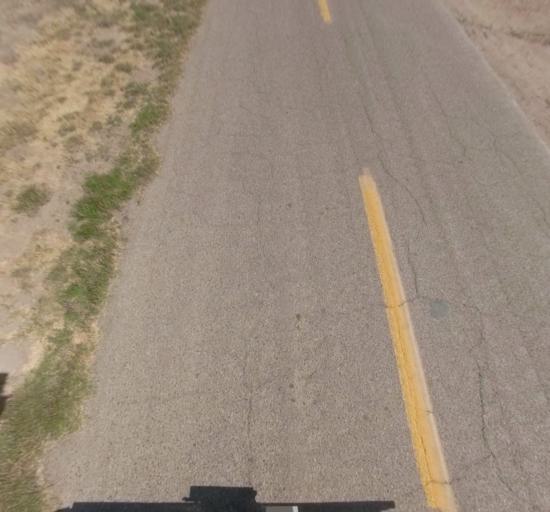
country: US
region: California
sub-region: Madera County
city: Parkwood
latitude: 36.8458
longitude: -120.1464
